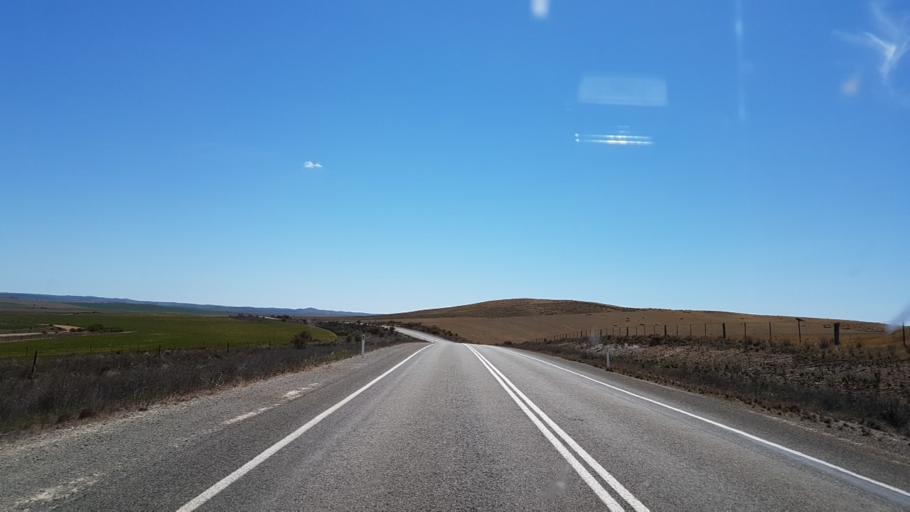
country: AU
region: South Australia
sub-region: Northern Areas
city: Jamestown
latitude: -33.3306
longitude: 138.8893
